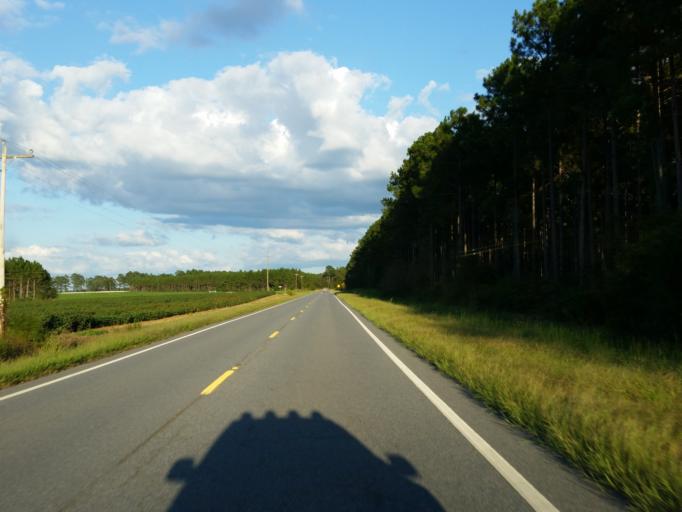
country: US
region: Georgia
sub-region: Dooly County
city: Vienna
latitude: 32.0862
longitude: -83.7218
